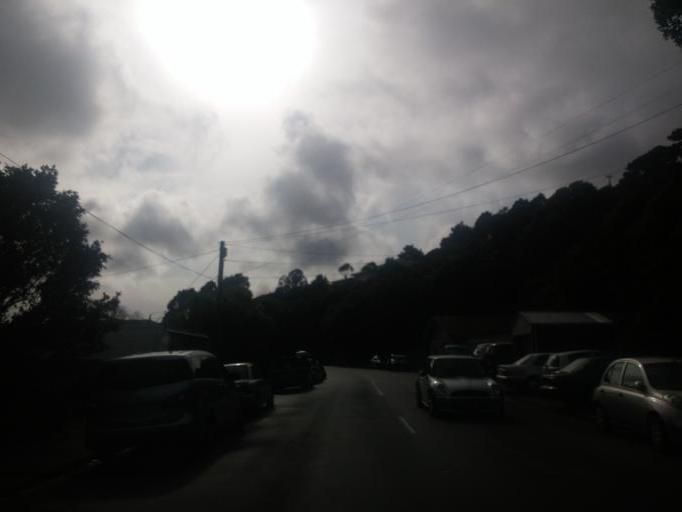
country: NZ
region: Wellington
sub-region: Wellington City
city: Kelburn
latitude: -41.2770
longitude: 174.7595
